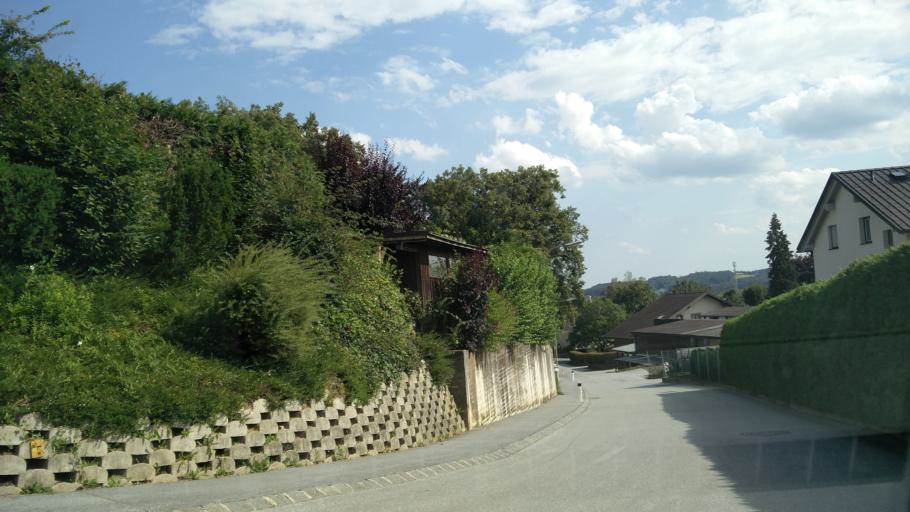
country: AT
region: Styria
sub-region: Politischer Bezirk Weiz
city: Weiz
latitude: 47.2232
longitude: 15.6311
